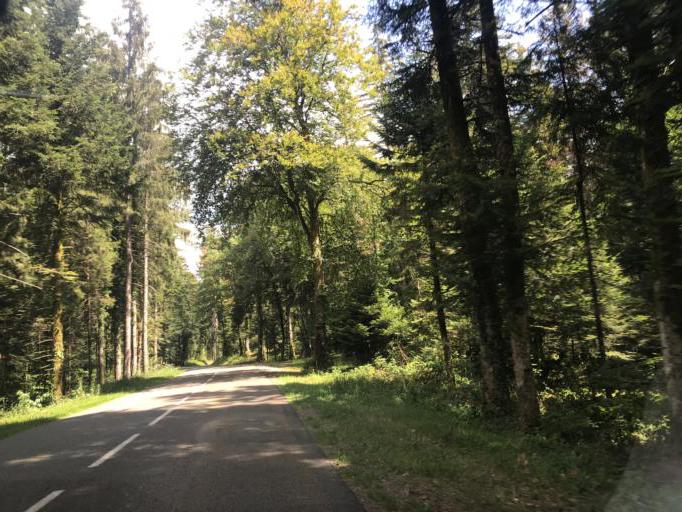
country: FR
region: Franche-Comte
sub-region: Departement du Jura
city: Clairvaux-les-Lacs
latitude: 46.5158
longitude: 5.7880
